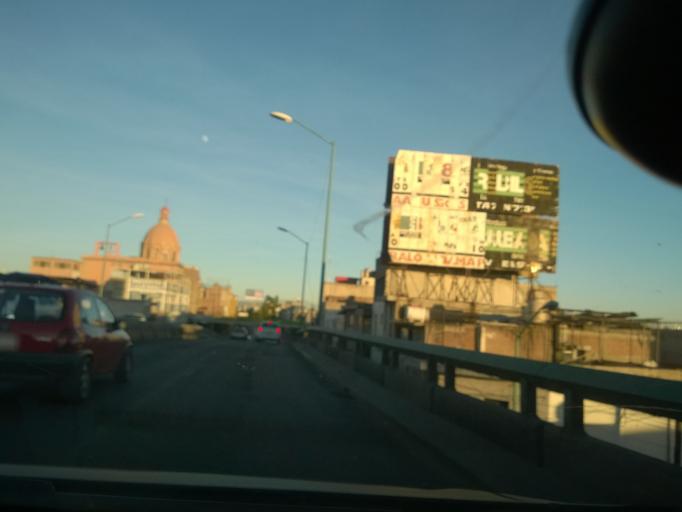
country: MX
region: Guanajuato
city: Leon
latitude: 21.1160
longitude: -101.6869
